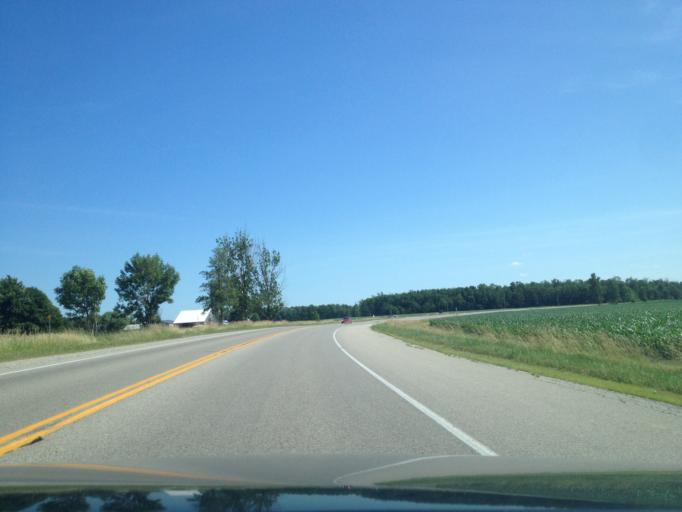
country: CA
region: Ontario
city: Stratford
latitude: 43.5013
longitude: -80.8804
